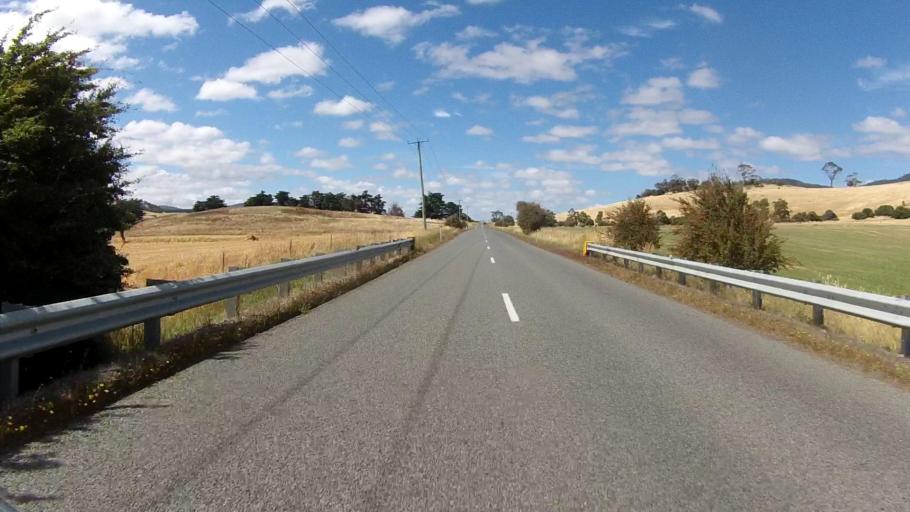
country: AU
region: Tasmania
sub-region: Brighton
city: Bridgewater
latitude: -42.5951
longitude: 147.4132
